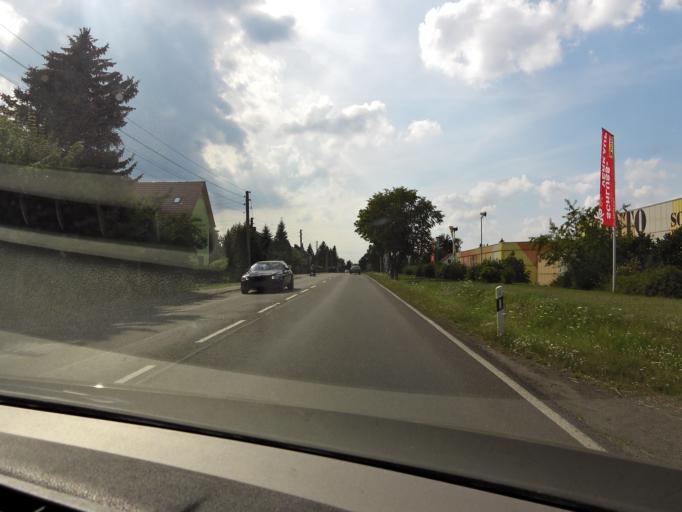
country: DE
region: Saxony
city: Grossposna
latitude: 51.2656
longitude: 12.4974
